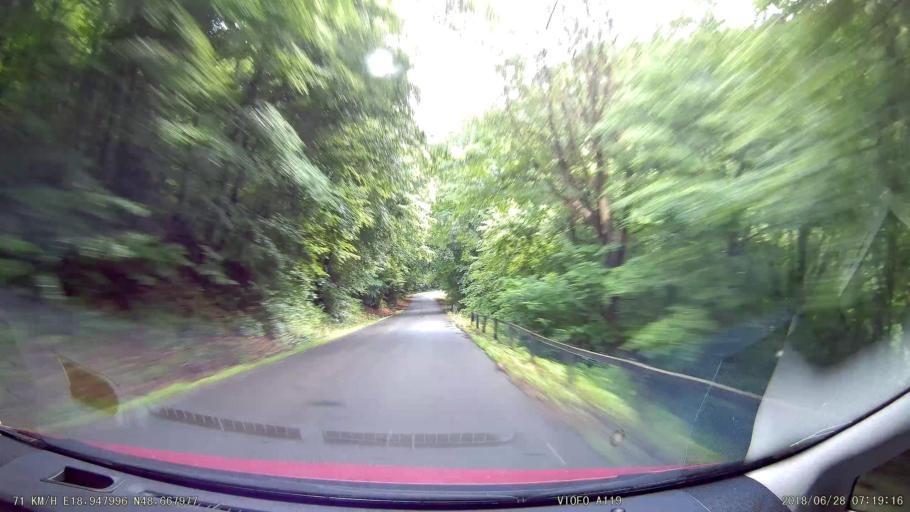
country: SK
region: Banskobystricky
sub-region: Okres Ziar nad Hronom
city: Kremnica
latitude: 48.6683
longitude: 18.9484
